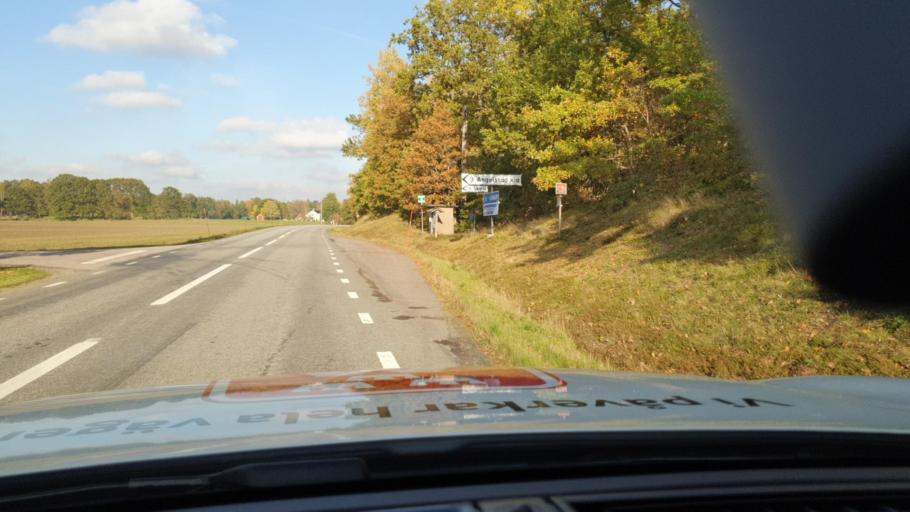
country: SE
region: Kronoberg
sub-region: Ljungby Kommun
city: Ljungby
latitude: 56.8204
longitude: 13.8019
